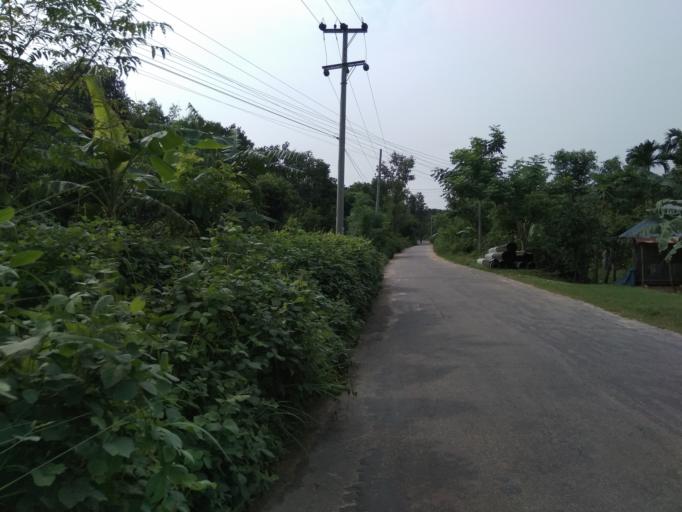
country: BD
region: Chittagong
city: Khagrachhari
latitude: 23.0374
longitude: 92.0045
